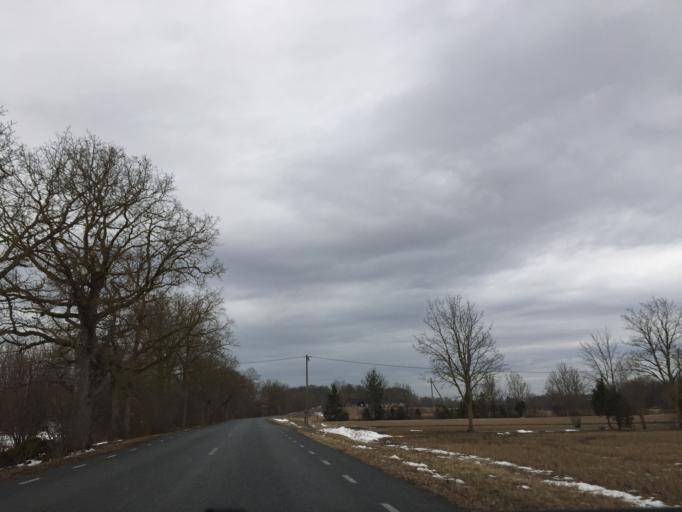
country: EE
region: Saare
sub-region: Orissaare vald
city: Orissaare
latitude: 58.5587
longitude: 22.7742
